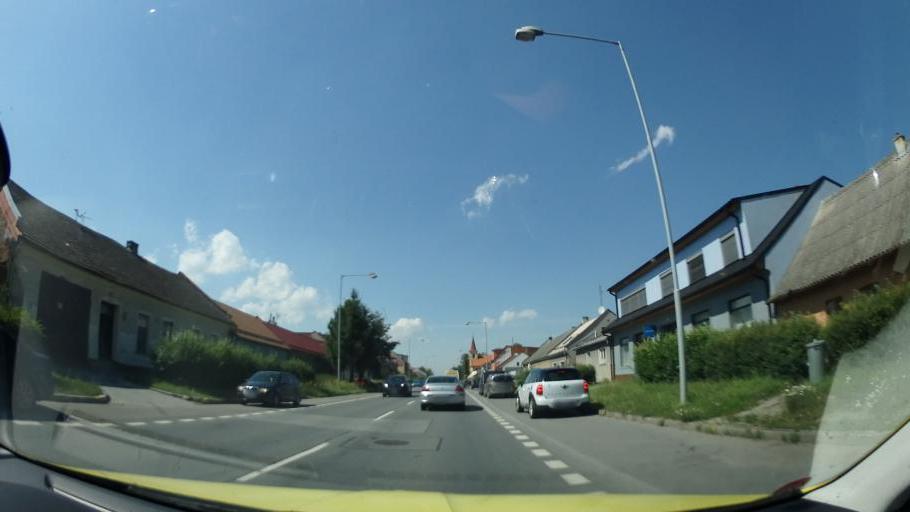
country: CZ
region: Olomoucky
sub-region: Okres Olomouc
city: Olomouc
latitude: 49.5661
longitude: 17.2621
